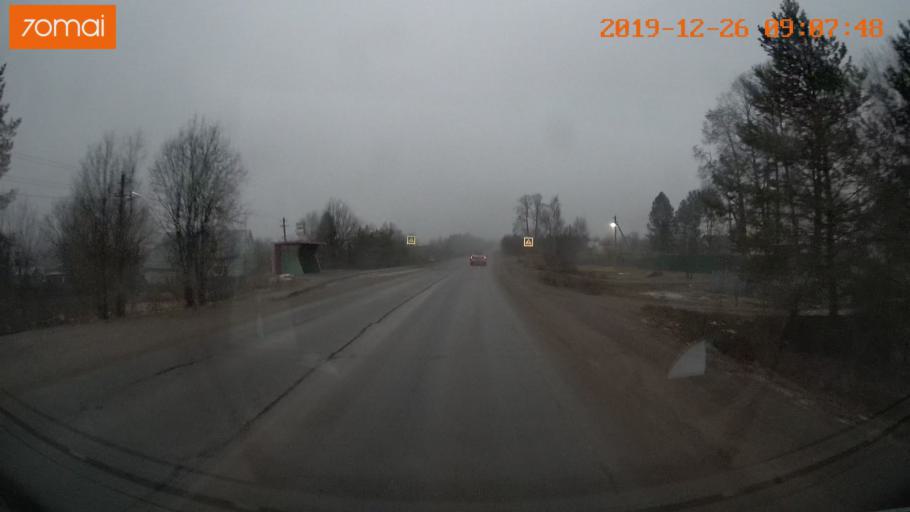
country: RU
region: Vologda
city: Gryazovets
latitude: 58.8500
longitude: 40.2468
